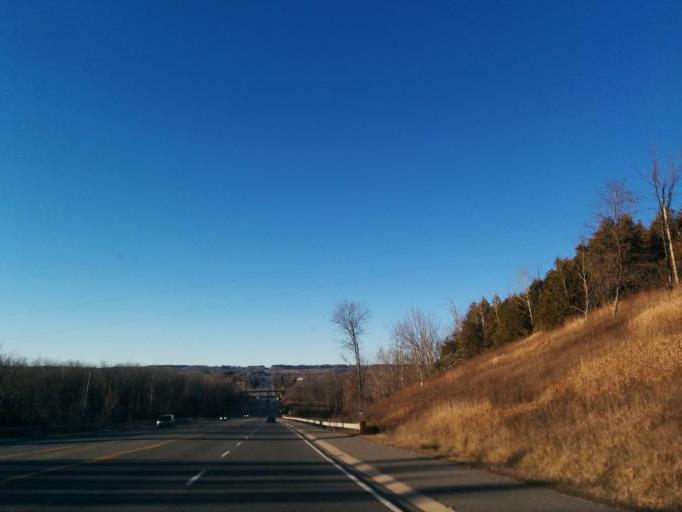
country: CA
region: Ontario
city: Brampton
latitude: 43.8078
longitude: -79.9250
